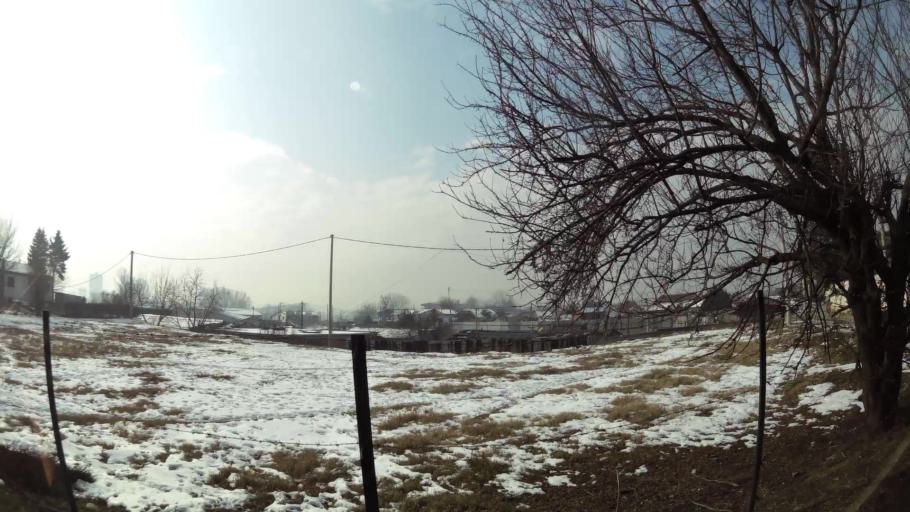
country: MK
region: Suto Orizari
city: Suto Orizare
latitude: 42.0156
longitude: 21.3874
